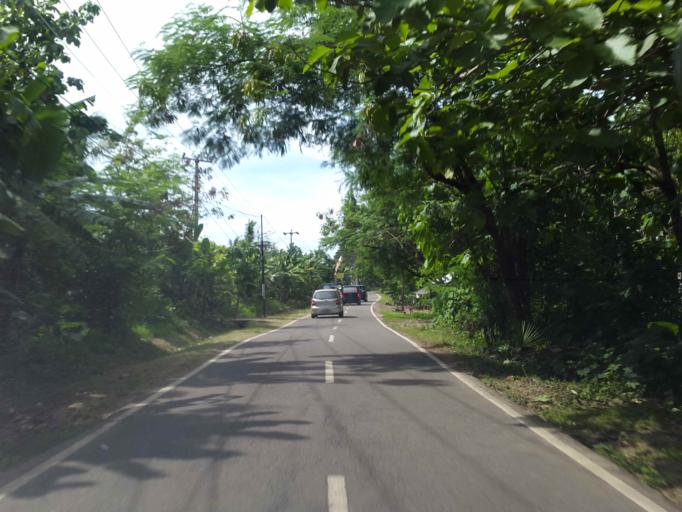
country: ID
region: Banten
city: Citeureup
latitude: -6.5109
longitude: 105.6728
